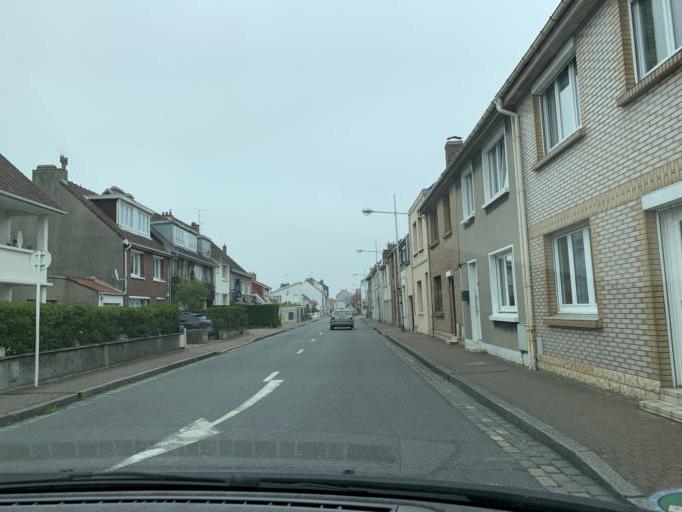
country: FR
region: Nord-Pas-de-Calais
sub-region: Departement du Pas-de-Calais
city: Coquelles
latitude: 50.9571
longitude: 1.8167
